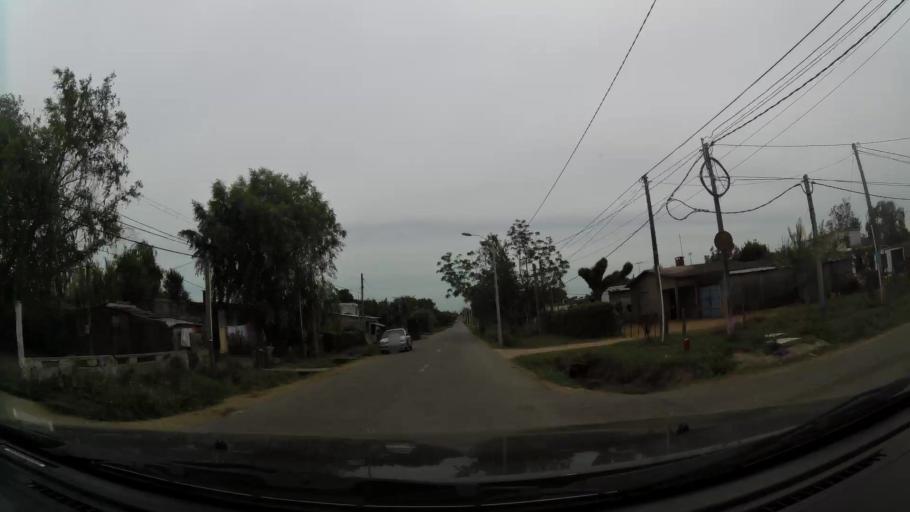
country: UY
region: Canelones
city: La Paz
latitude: -34.7432
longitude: -56.2315
